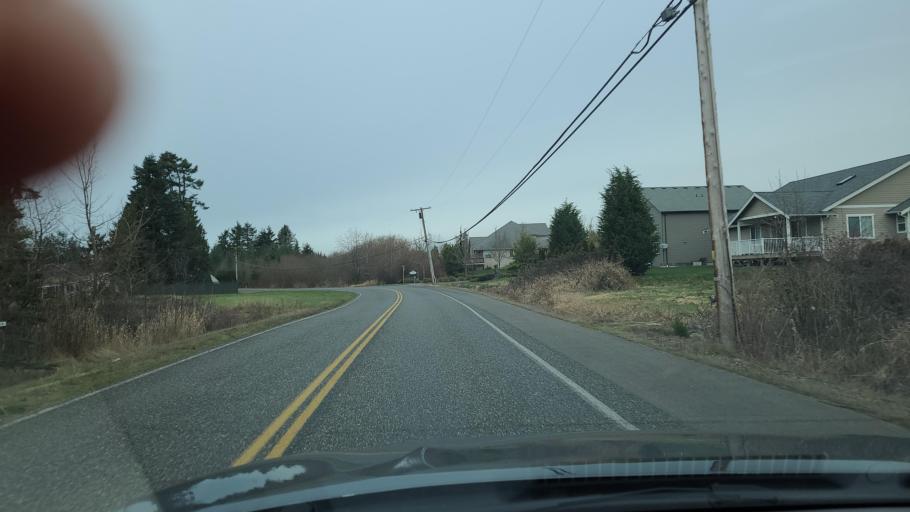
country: US
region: Washington
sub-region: Whatcom County
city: Birch Bay
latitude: 48.9536
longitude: -122.7199
